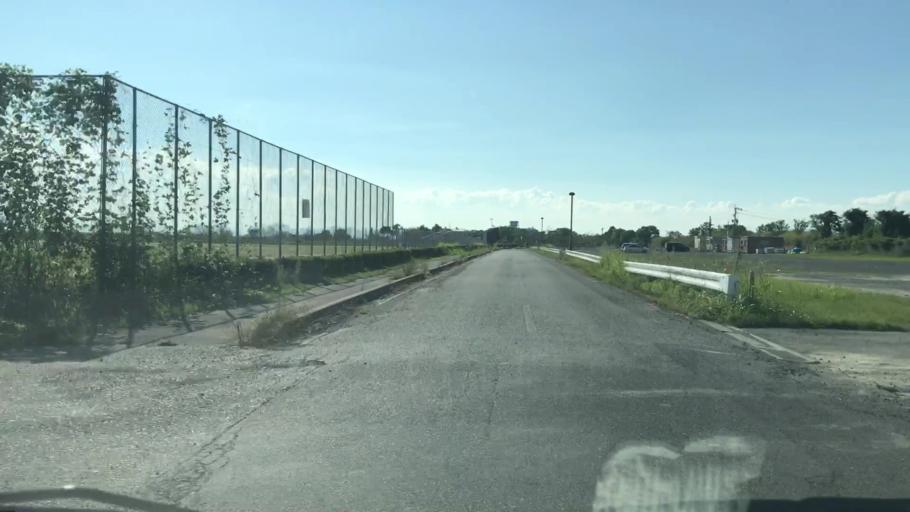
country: JP
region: Saga Prefecture
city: Okawa
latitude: 33.1519
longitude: 130.3134
